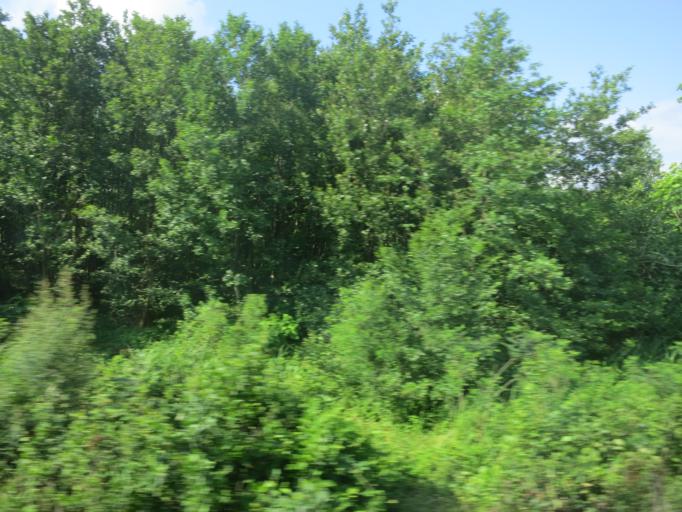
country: GE
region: Guria
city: Lanchkhuti
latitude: 42.0897
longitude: 42.0524
